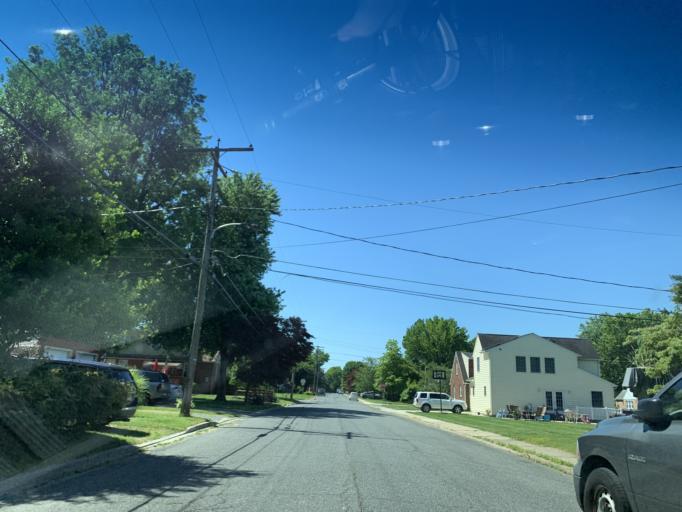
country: US
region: Maryland
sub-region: Harford County
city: Havre de Grace
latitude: 39.5421
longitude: -76.0951
